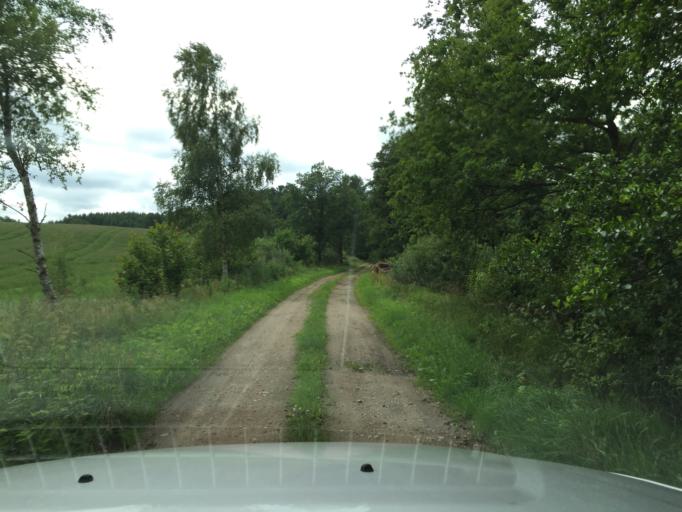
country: SE
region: Skane
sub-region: Hassleholms Kommun
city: Sosdala
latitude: 56.0330
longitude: 13.6933
